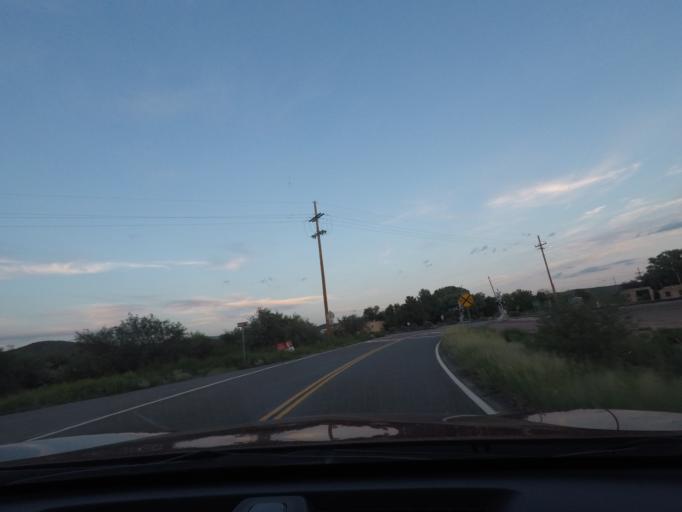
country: US
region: Arizona
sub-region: Yavapai County
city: Prescott
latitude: 34.4178
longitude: -112.7110
